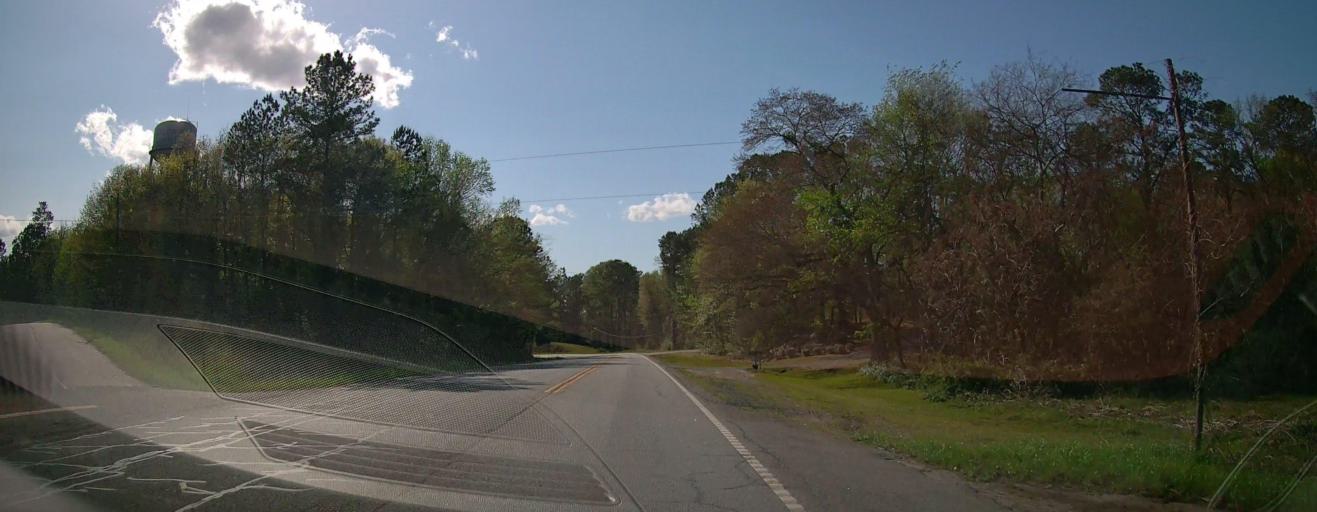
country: US
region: Georgia
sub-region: Baldwin County
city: Hardwick
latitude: 33.0916
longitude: -83.1818
